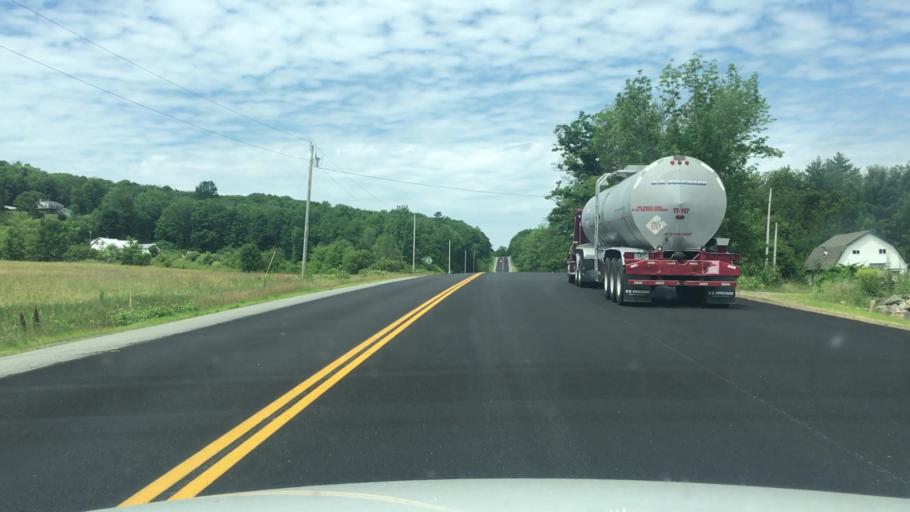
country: US
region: Maine
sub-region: Waldo County
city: Searsmont
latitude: 44.4024
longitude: -69.2971
